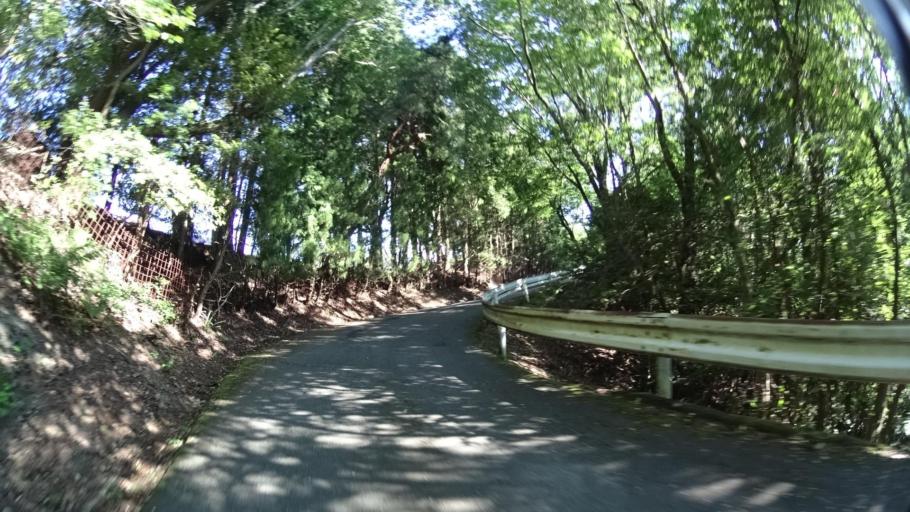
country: JP
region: Kyoto
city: Kameoka
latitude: 34.9885
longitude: 135.5606
